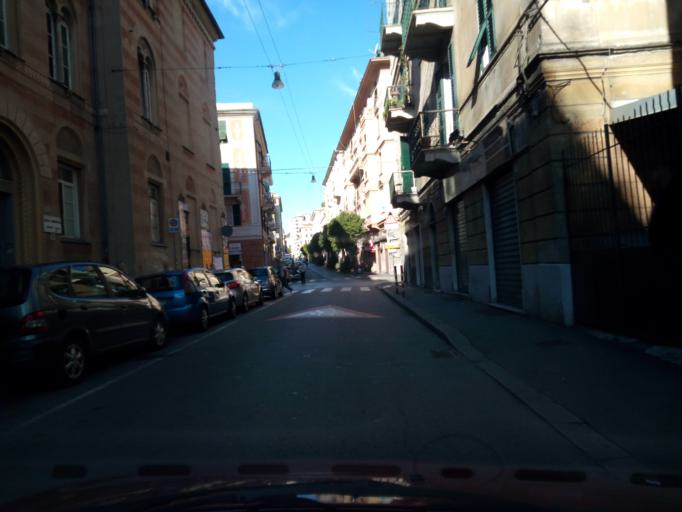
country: IT
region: Liguria
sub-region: Provincia di Genova
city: Mele
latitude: 44.4258
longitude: 8.8202
